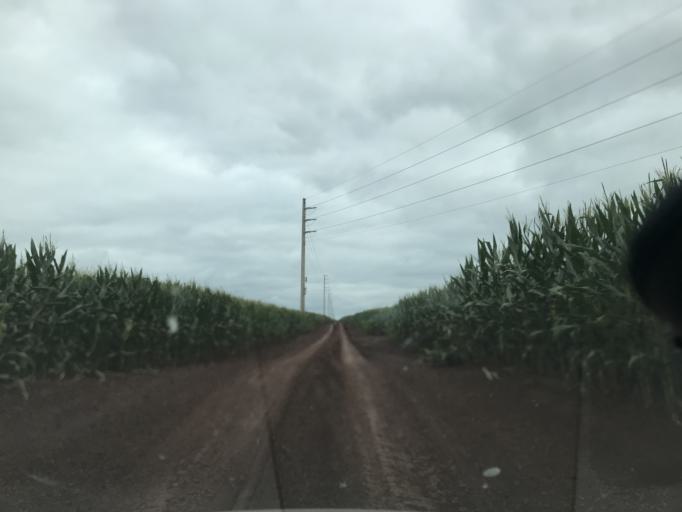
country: BR
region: Parana
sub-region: Palotina
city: Palotina
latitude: -24.2989
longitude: -53.8171
